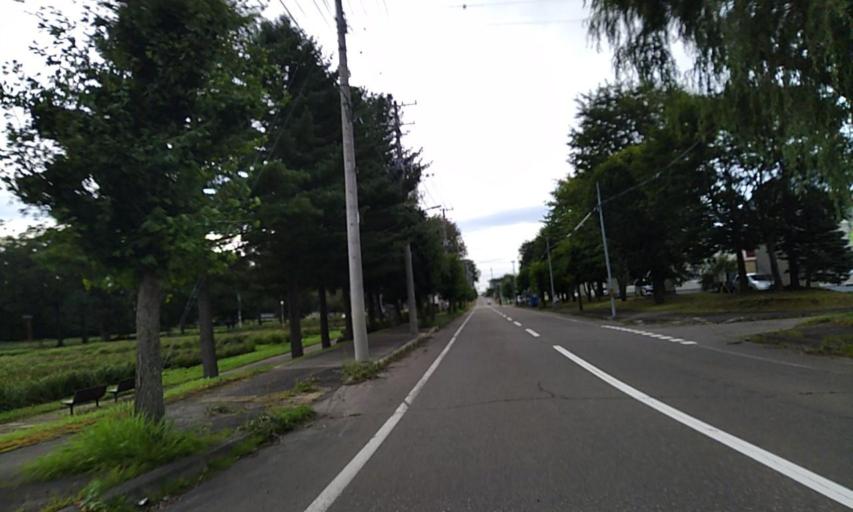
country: JP
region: Hokkaido
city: Obihiro
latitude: 42.9201
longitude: 143.0418
